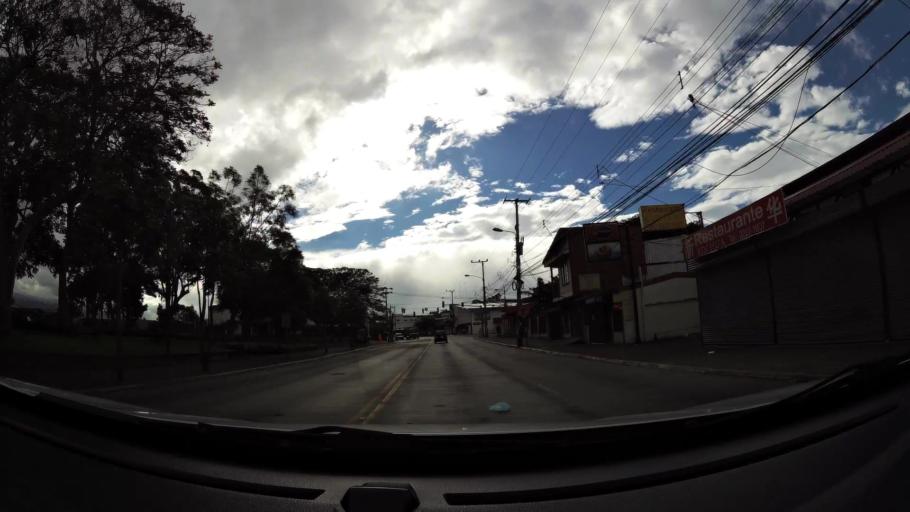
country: CR
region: San Jose
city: San Pedro
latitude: 9.9106
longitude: -84.0574
